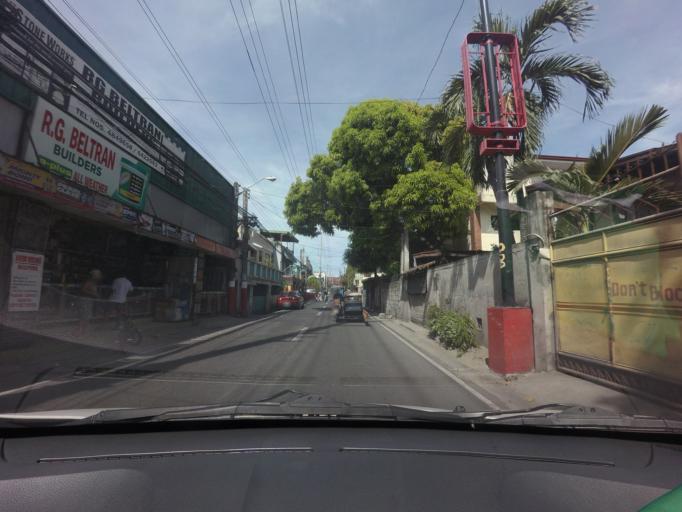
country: PH
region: Calabarzon
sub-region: Province of Rizal
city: Taguig
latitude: 14.5282
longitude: 121.0757
